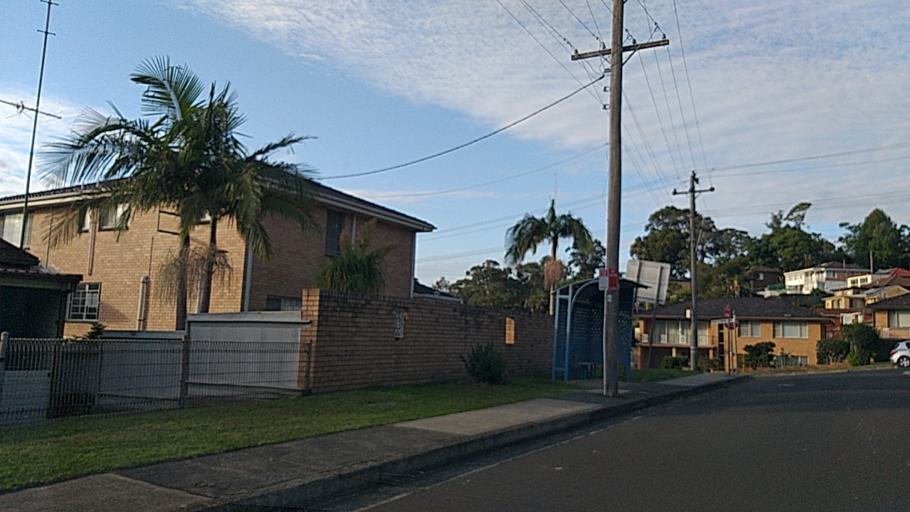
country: AU
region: New South Wales
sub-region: Wollongong
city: Mount Ousley
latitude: -34.3876
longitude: 150.8726
